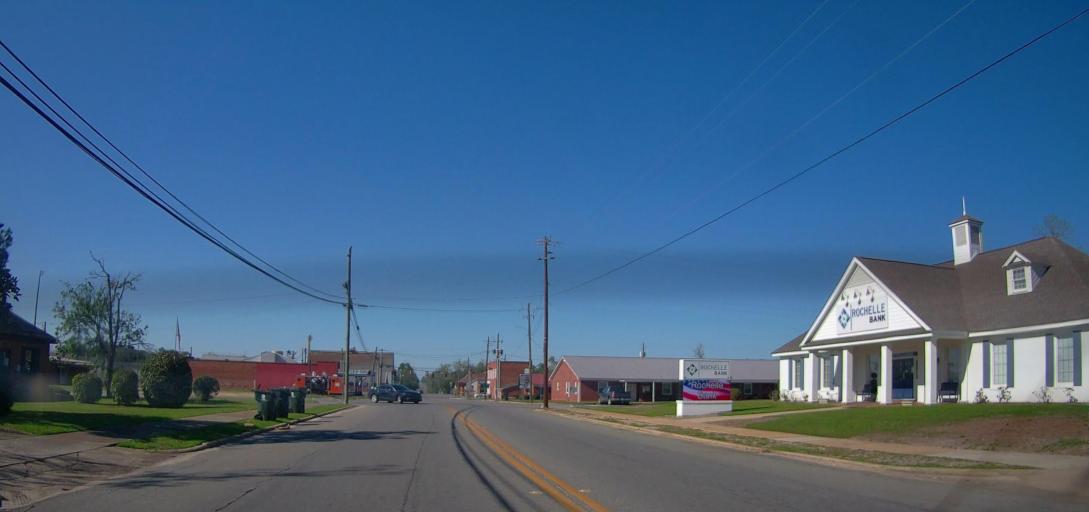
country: US
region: Georgia
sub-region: Wilcox County
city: Rochelle
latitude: 31.9494
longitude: -83.4562
